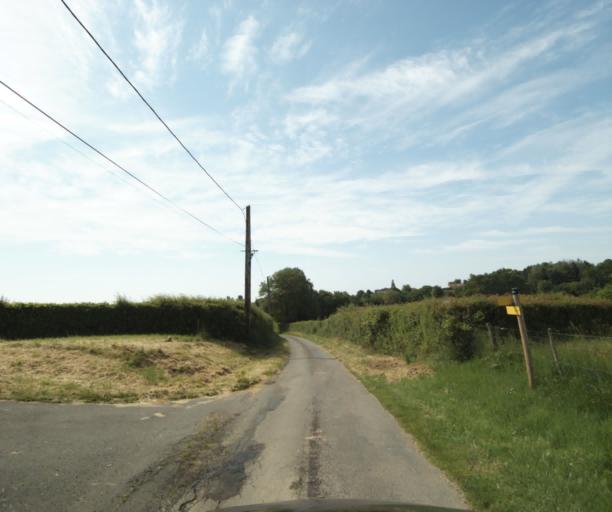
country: FR
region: Bourgogne
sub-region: Departement de Saone-et-Loire
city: Gueugnon
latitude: 46.5423
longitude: 4.1232
